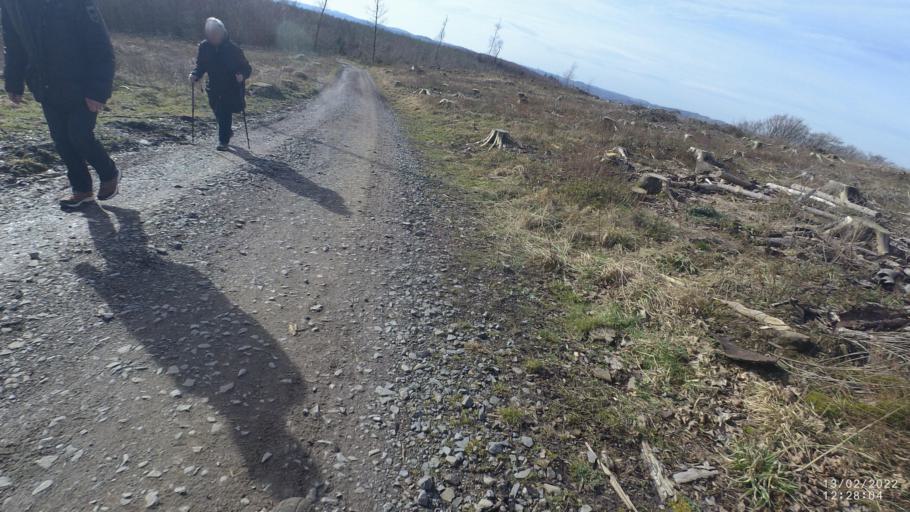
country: DE
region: North Rhine-Westphalia
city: Neuenrade
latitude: 51.2857
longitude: 7.7564
